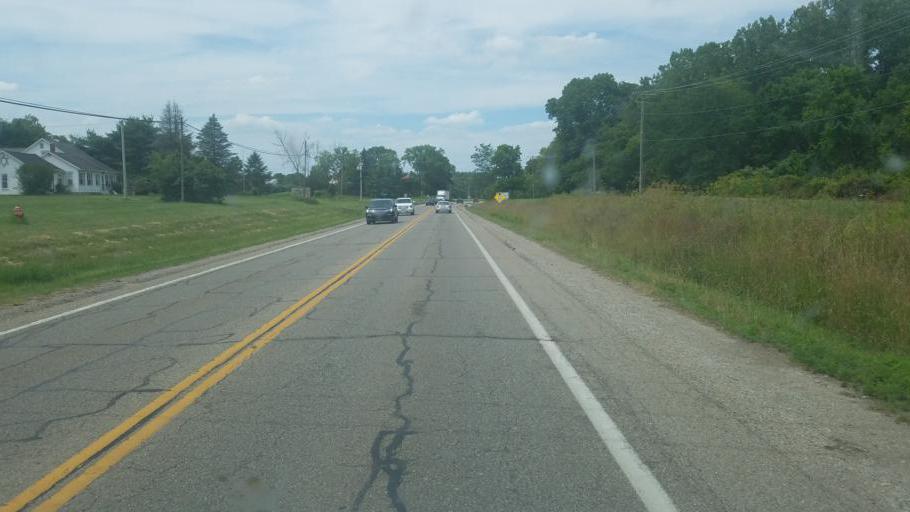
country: US
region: Ohio
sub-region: Knox County
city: Mount Vernon
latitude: 40.3896
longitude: -82.5070
